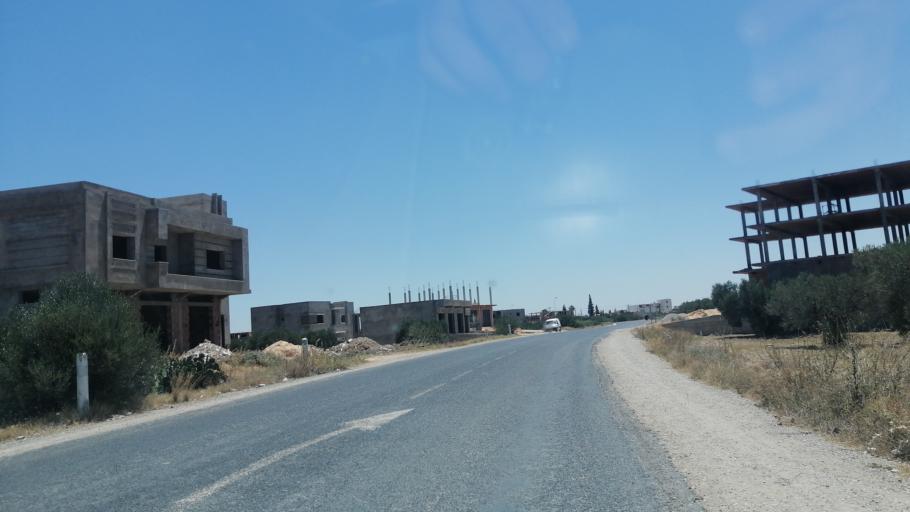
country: TN
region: Al Qayrawan
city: Sbikha
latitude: 36.1314
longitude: 10.0917
